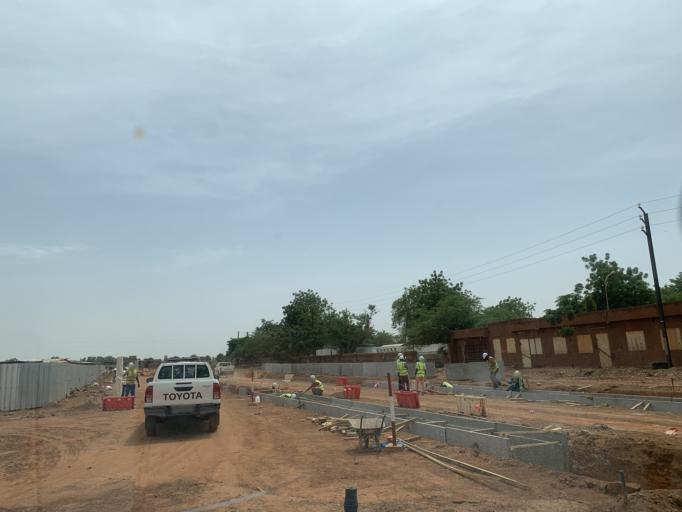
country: BF
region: Centre
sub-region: Kadiogo Province
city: Ouagadougou
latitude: 12.3345
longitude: -1.5158
